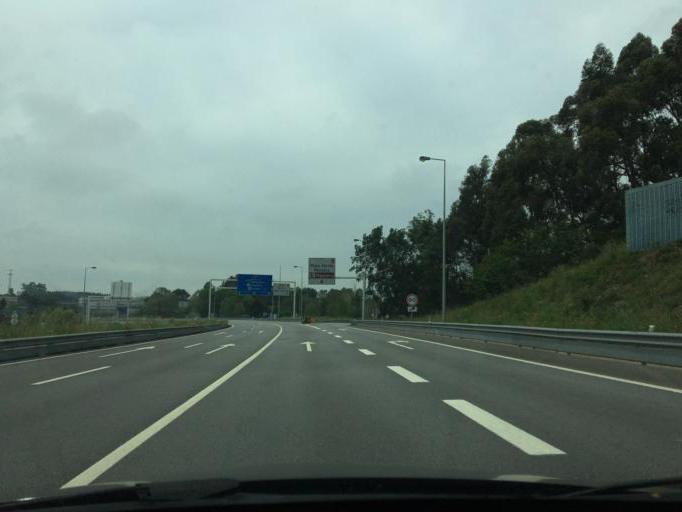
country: PT
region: Porto
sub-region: Maia
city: Maia
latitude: 41.2406
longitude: -8.6434
